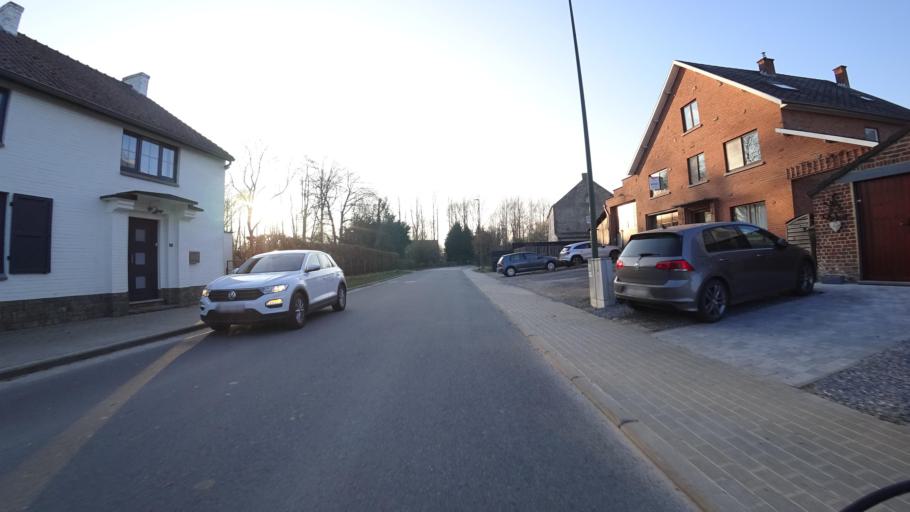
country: BE
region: Wallonia
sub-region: Province du Brabant Wallon
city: Chastre
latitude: 50.5803
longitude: 4.6419
